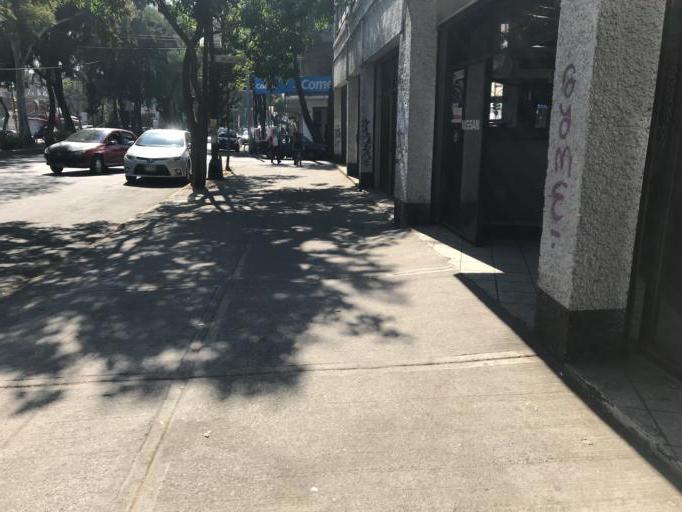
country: MX
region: Mexico City
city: Colonia Nativitas
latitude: 19.4011
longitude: -99.1249
